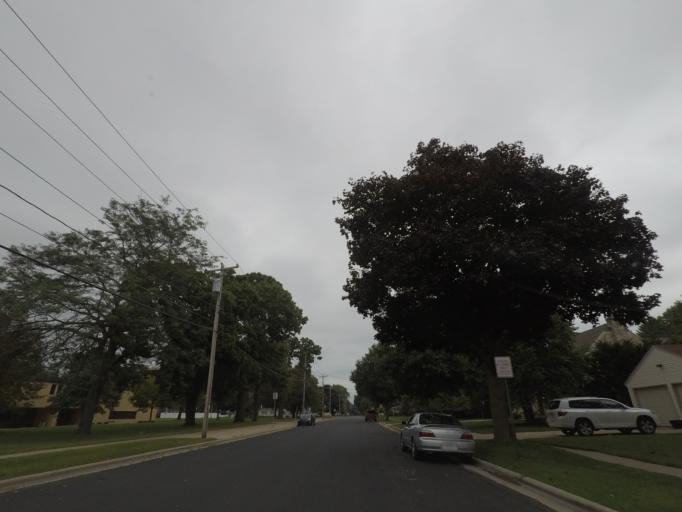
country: US
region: Wisconsin
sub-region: Dane County
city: Middleton
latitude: 43.0982
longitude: -89.5082
